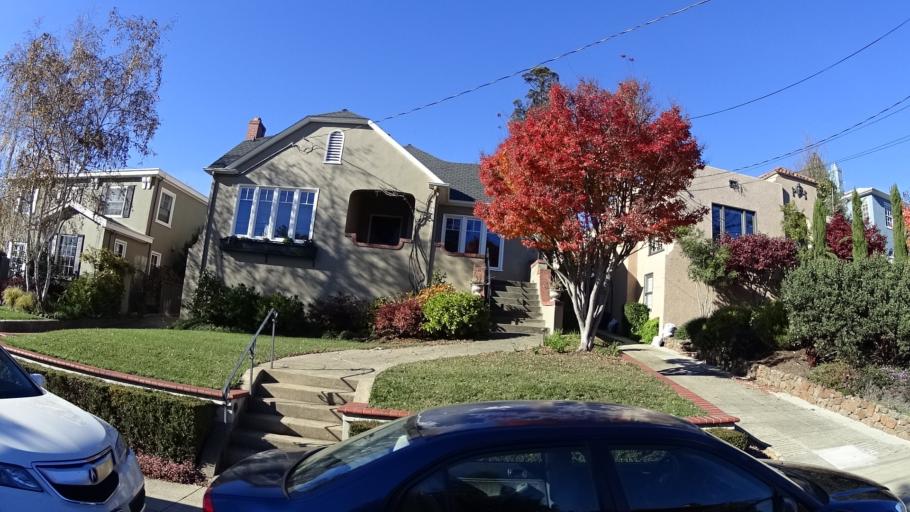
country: US
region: California
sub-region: Alameda County
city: Piedmont
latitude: 37.8130
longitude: -122.2246
